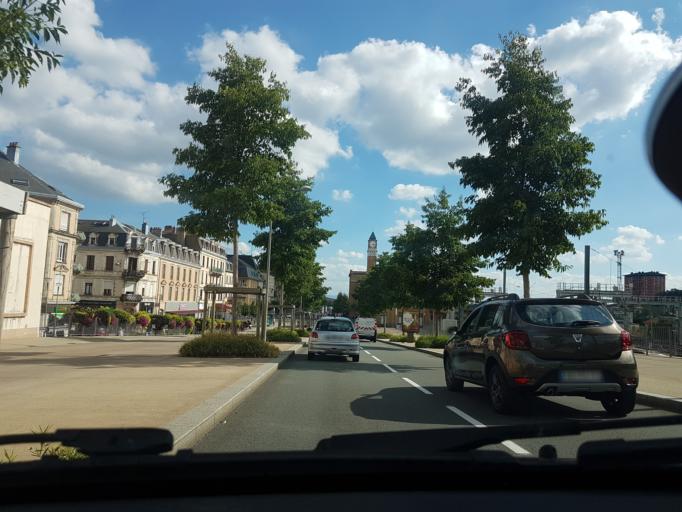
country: FR
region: Franche-Comte
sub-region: Territoire de Belfort
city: Belfort
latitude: 47.6352
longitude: 6.8531
